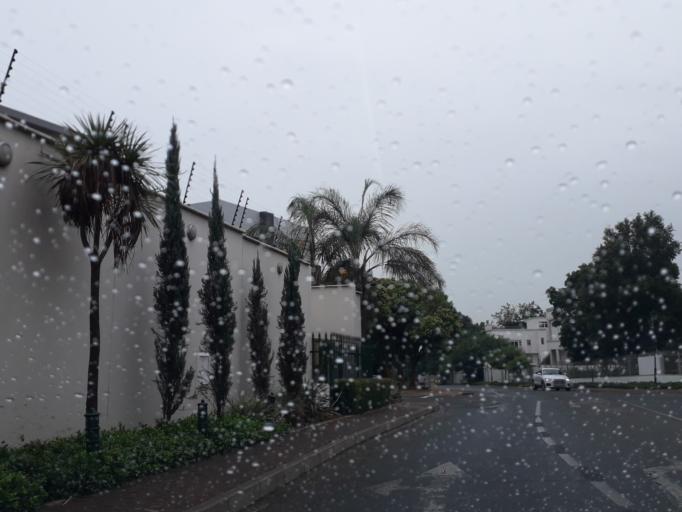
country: ZA
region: Gauteng
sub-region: City of Johannesburg Metropolitan Municipality
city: Johannesburg
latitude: -26.1351
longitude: 28.0445
